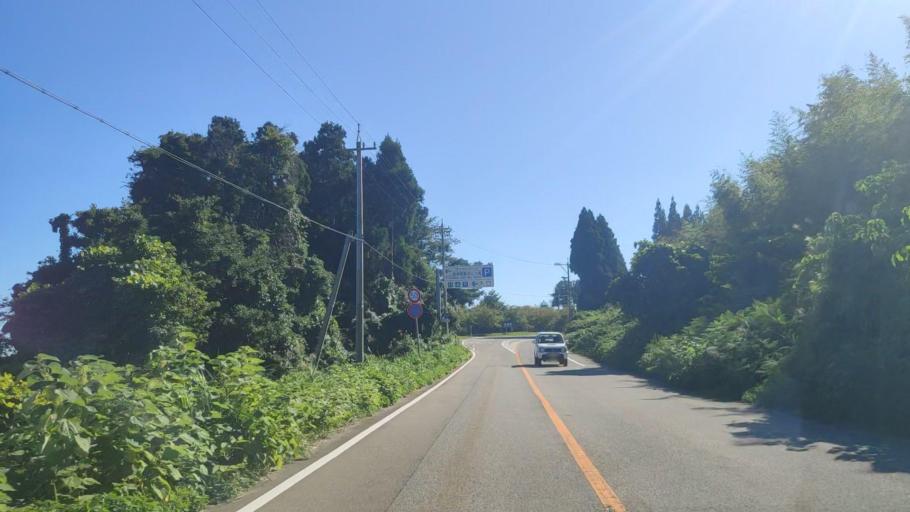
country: JP
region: Ishikawa
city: Nanao
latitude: 37.2689
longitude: 137.0947
